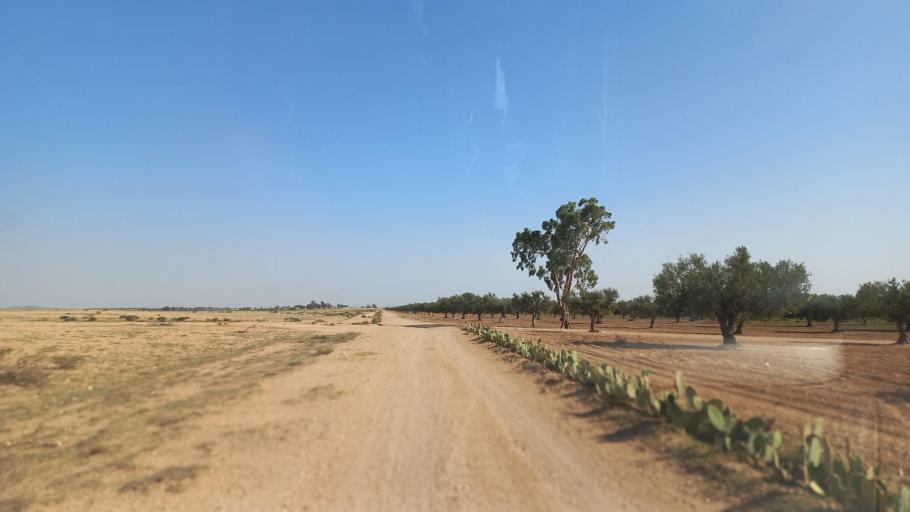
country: TN
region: Al Qasrayn
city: Kasserine
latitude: 35.3083
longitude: 9.0208
